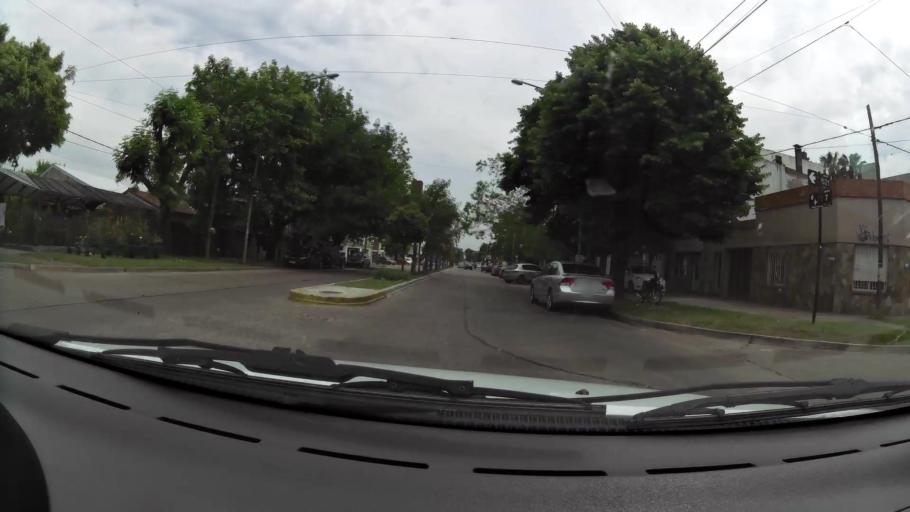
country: AR
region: Buenos Aires
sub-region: Partido de La Plata
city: La Plata
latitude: -34.8912
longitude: -57.9813
